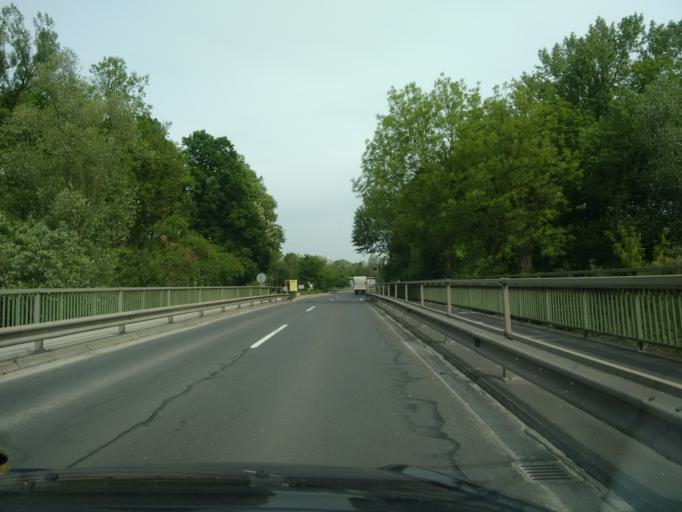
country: AT
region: Upper Austria
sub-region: Politischer Bezirk Linz-Land
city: Traun
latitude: 48.2139
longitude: 14.2409
